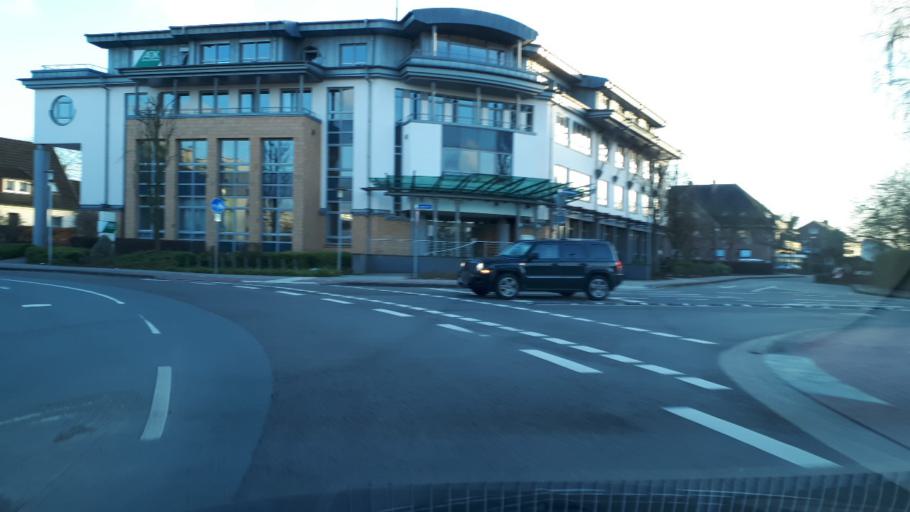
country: DE
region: Lower Saxony
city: Cloppenburg
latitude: 52.8420
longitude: 8.0452
